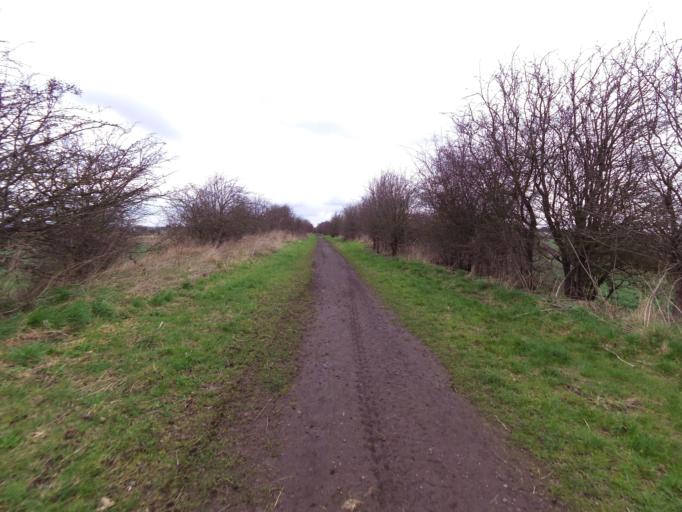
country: GB
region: England
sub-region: Doncaster
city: Bentley
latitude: 53.5515
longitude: -1.1560
